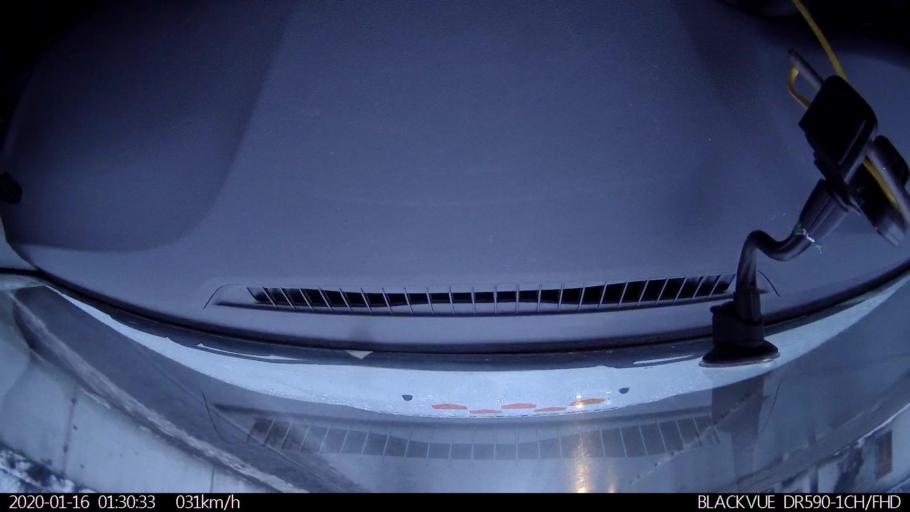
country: RU
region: Nizjnij Novgorod
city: Gorbatovka
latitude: 56.3413
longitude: 43.8194
